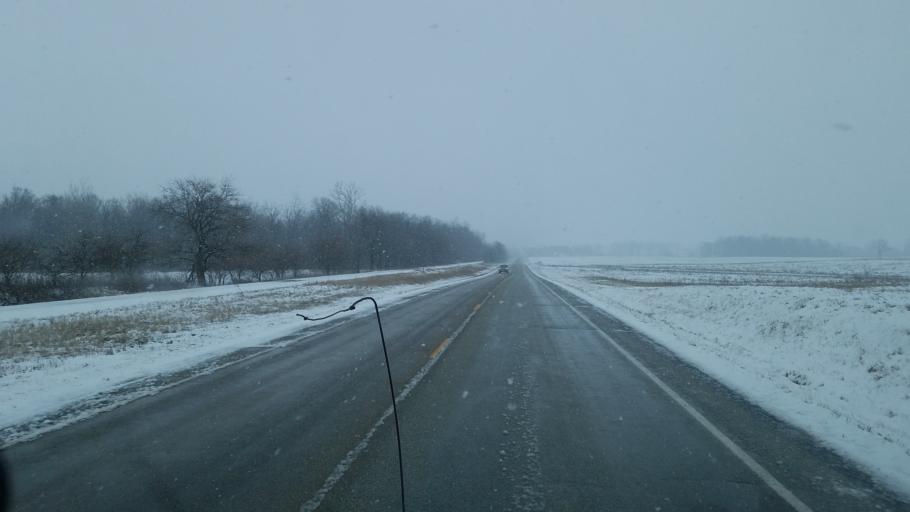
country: US
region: Indiana
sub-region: Wayne County
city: Hagerstown
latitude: 39.9734
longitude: -85.0479
